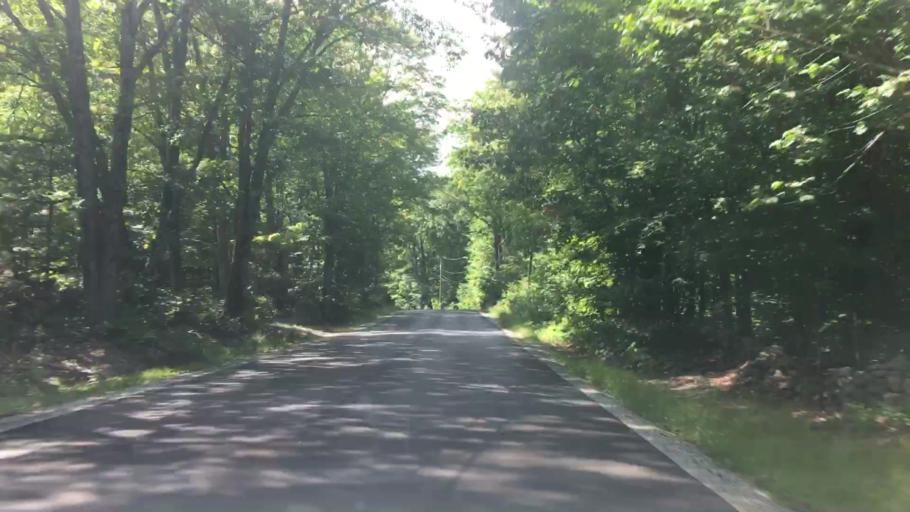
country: US
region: Maine
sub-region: Androscoggin County
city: Poland
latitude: 44.0119
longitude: -70.4088
